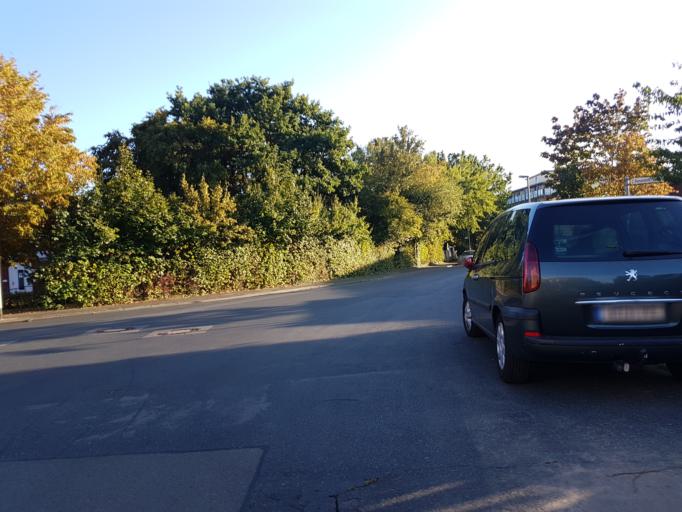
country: DE
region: Lower Saxony
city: Langenhagen
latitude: 52.4161
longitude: 9.7610
